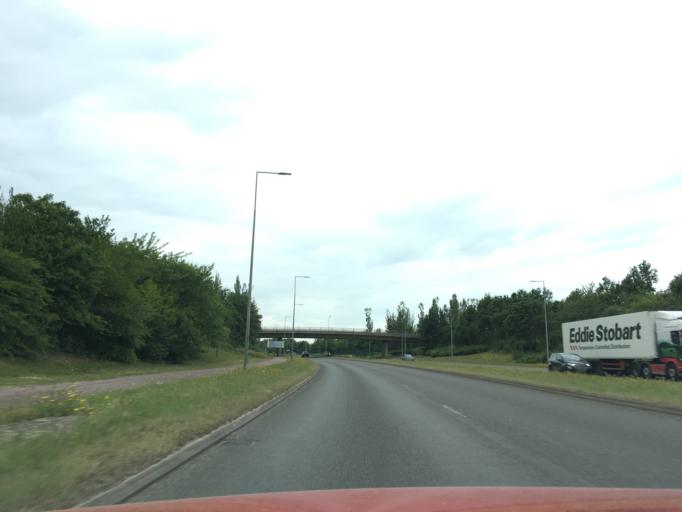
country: GB
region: England
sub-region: Milton Keynes
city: Broughton
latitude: 52.0452
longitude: -0.6987
